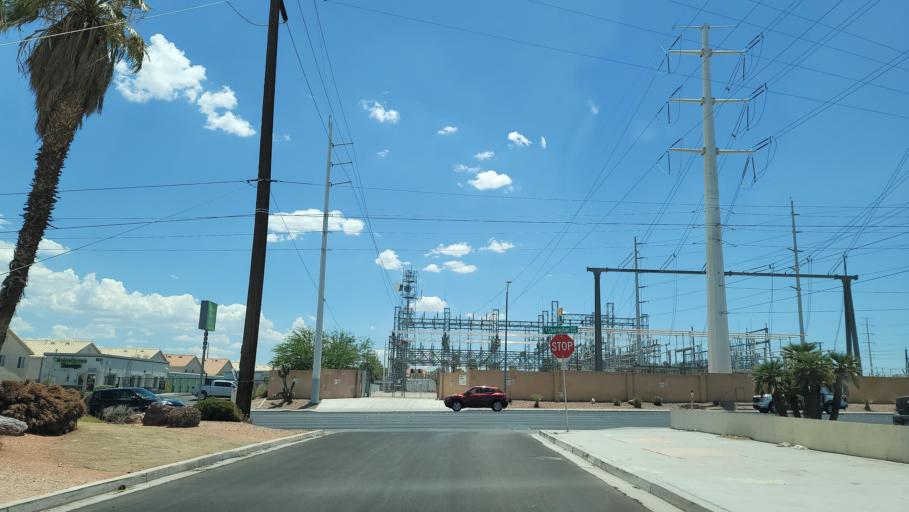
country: US
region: Nevada
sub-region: Clark County
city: Spring Valley
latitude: 36.1594
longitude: -115.2779
